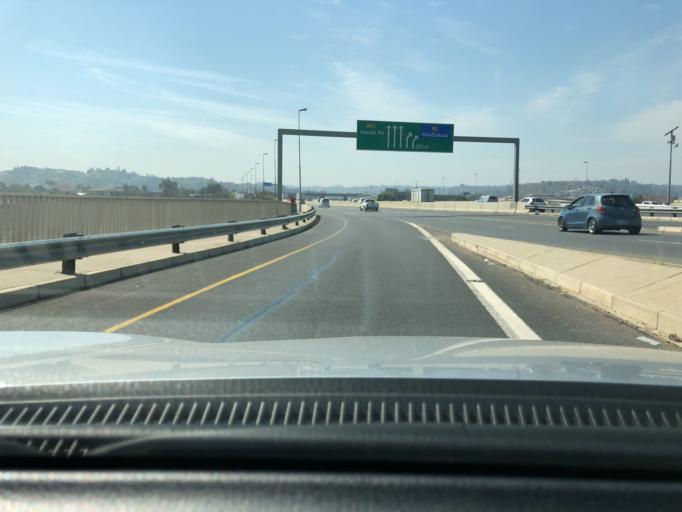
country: ZA
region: KwaZulu-Natal
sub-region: eThekwini Metropolitan Municipality
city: Berea
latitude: -29.8051
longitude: 30.9784
